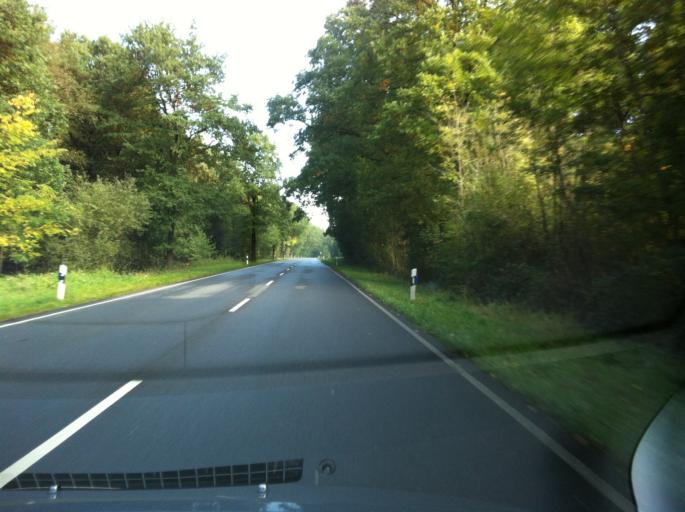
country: DE
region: Lower Saxony
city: Bad Bentheim
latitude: 52.2635
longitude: 7.1674
